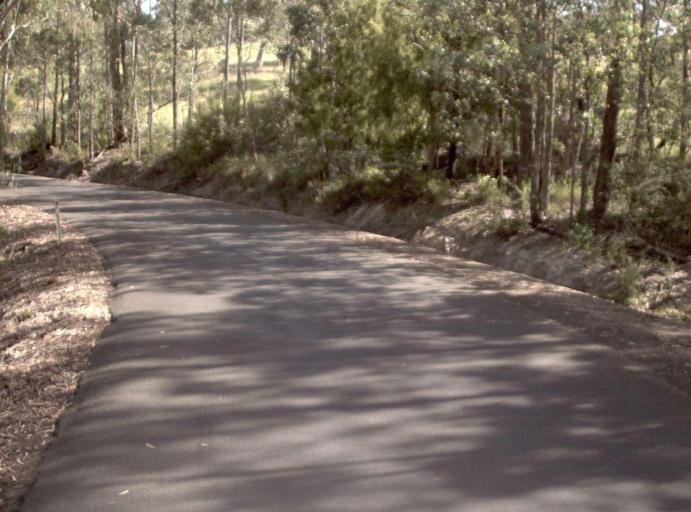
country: AU
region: Victoria
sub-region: East Gippsland
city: Lakes Entrance
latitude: -37.4747
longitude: 148.1256
